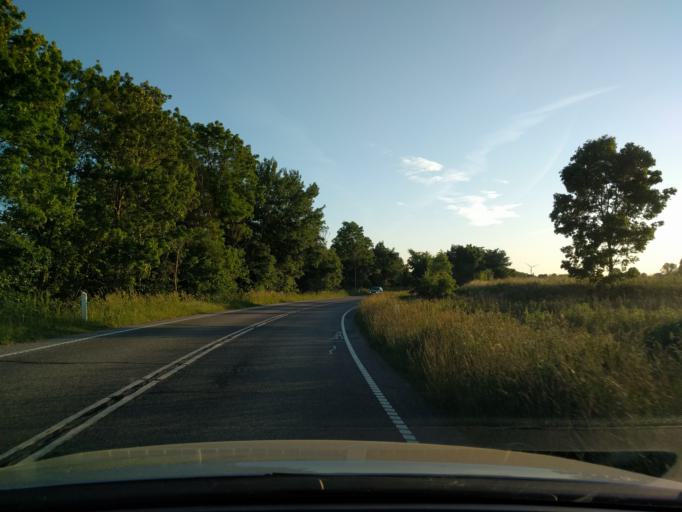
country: DK
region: South Denmark
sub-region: Kerteminde Kommune
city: Kerteminde
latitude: 55.4783
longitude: 10.6139
